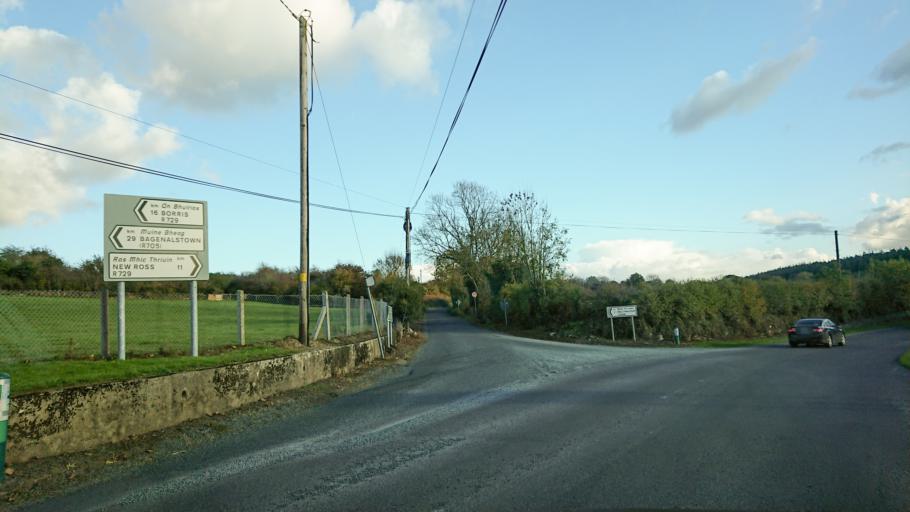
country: IE
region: Leinster
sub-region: Loch Garman
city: New Ross
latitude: 52.4712
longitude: -6.9005
